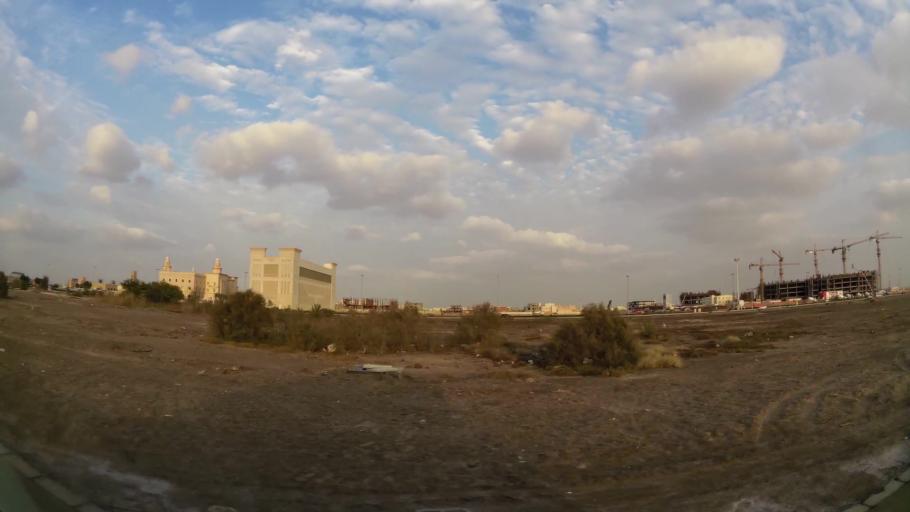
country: AE
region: Abu Dhabi
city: Abu Dhabi
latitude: 24.3576
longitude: 54.5350
